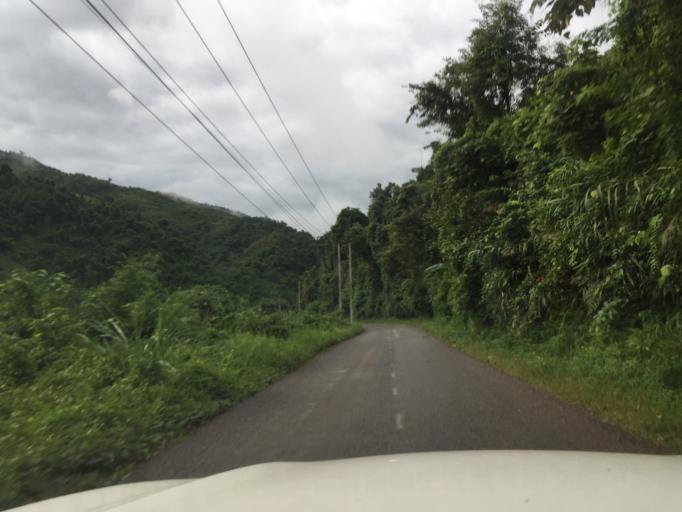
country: LA
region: Oudomxai
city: Muang La
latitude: 21.0608
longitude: 102.2408
